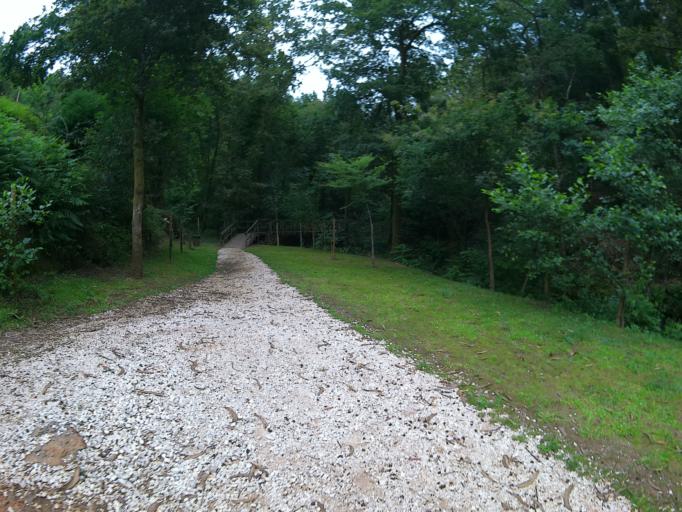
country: PT
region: Aveiro
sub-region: Albergaria-A-Velha
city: Branca
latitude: 40.7435
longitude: -8.4395
